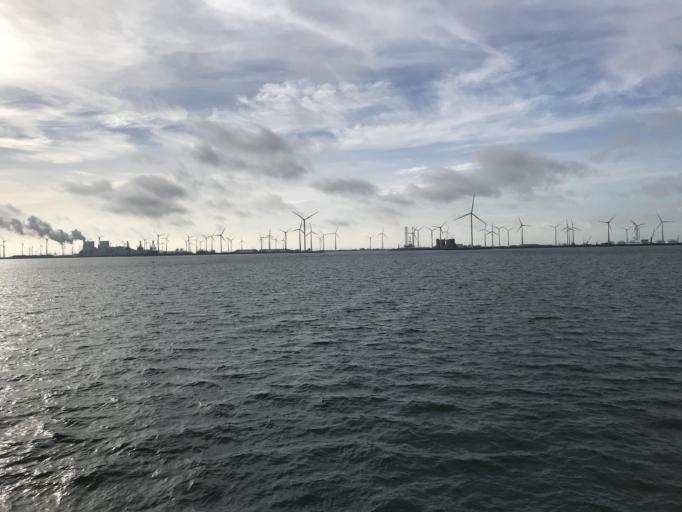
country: NL
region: Groningen
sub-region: Gemeente Appingedam
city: Appingedam
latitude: 53.4799
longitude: 6.8463
